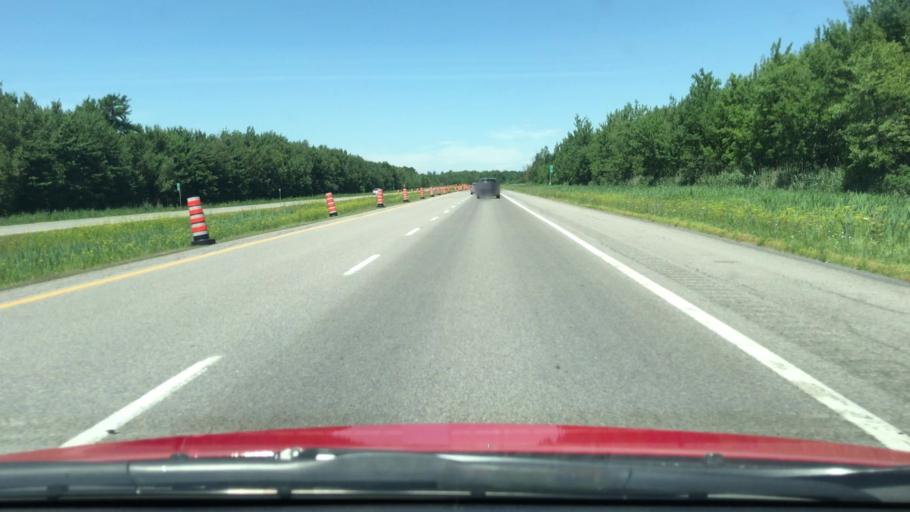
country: CA
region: Quebec
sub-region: Monteregie
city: Napierville
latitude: 45.1554
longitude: -73.4677
